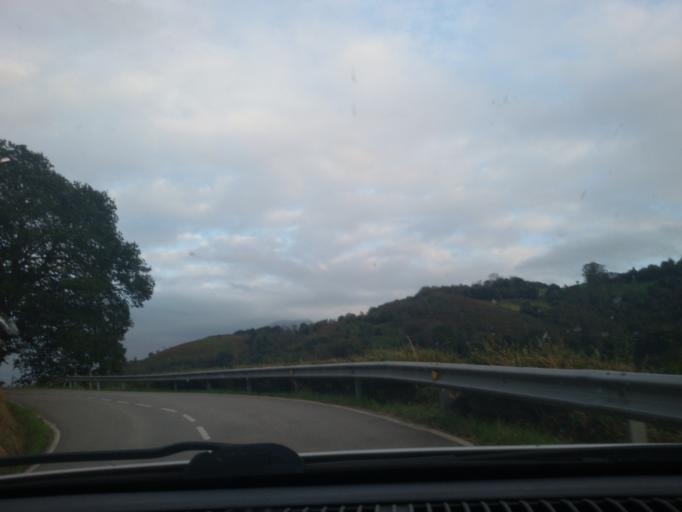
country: ES
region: Asturias
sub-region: Province of Asturias
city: Bimenes
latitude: 43.3346
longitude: -5.5878
